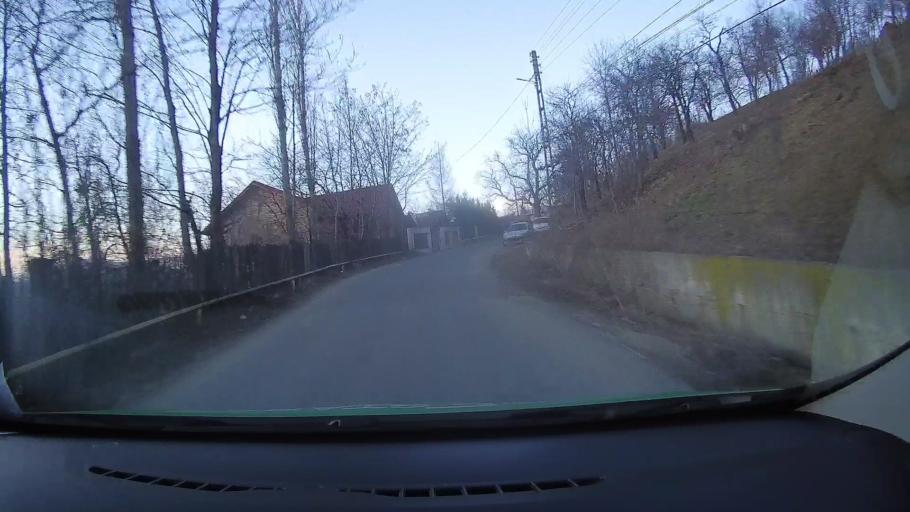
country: RO
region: Prahova
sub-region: Comuna Comarnic
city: Comarnic
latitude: 45.2477
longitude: 25.6418
